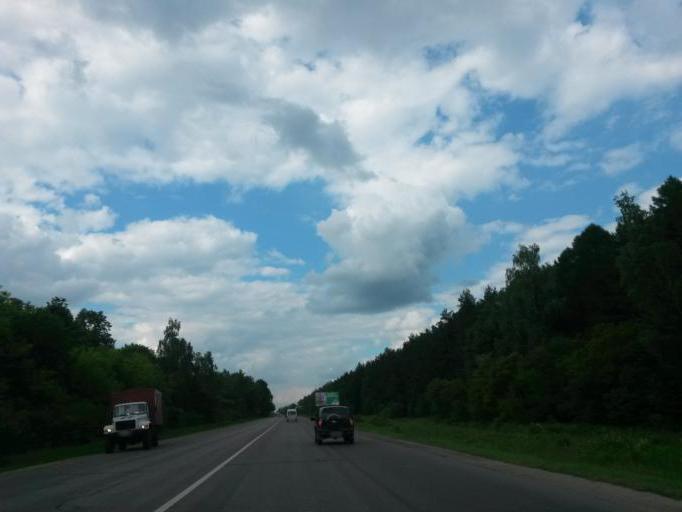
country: RU
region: Moskovskaya
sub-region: Chekhovskiy Rayon
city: Chekhov
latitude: 55.1904
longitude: 37.5019
